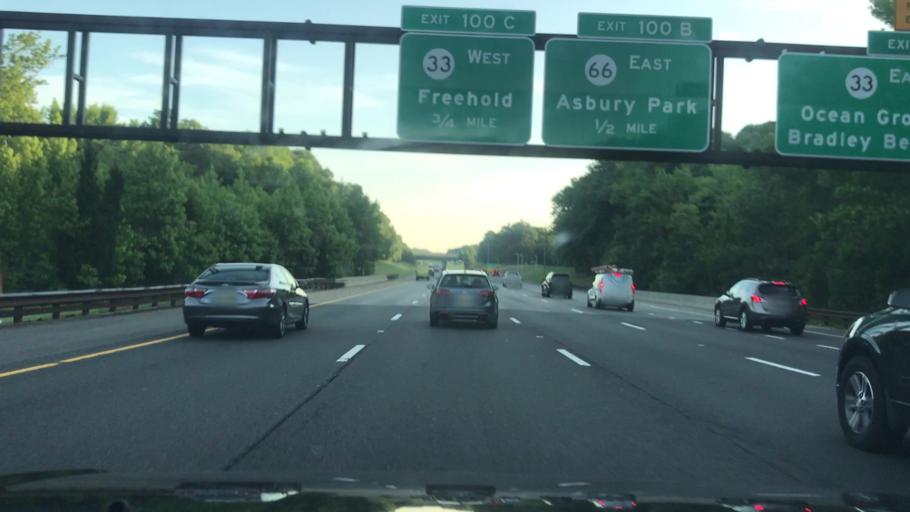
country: US
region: New Jersey
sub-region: Monmouth County
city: Shark River Hills
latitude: 40.2073
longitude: -74.0973
